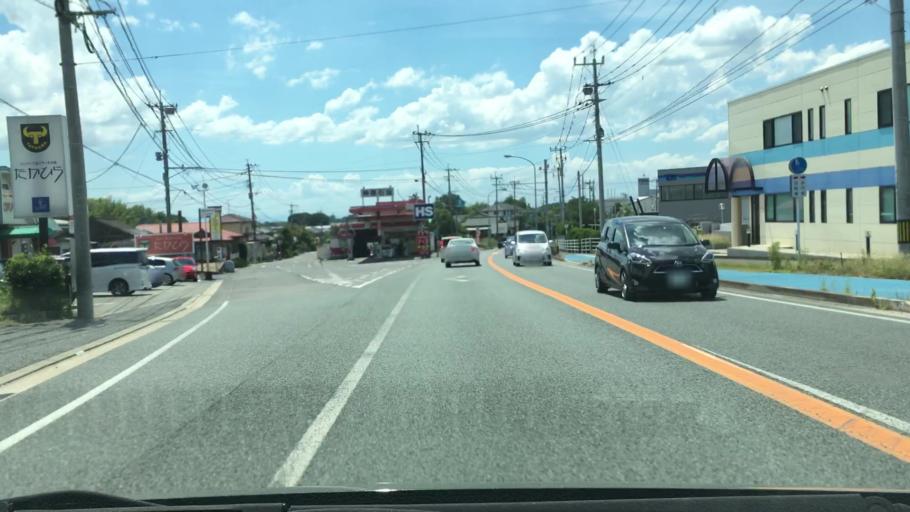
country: JP
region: Saga Prefecture
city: Tosu
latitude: 33.3480
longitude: 130.4581
